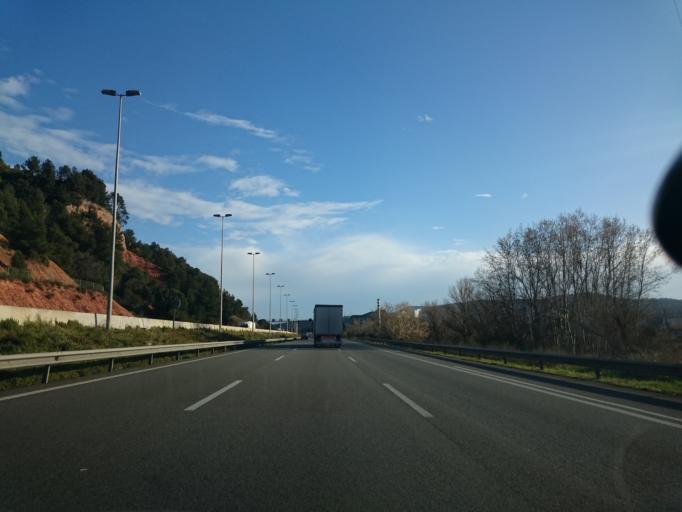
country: ES
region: Catalonia
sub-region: Provincia de Barcelona
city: Castellbisbal
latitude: 41.4620
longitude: 1.9803
